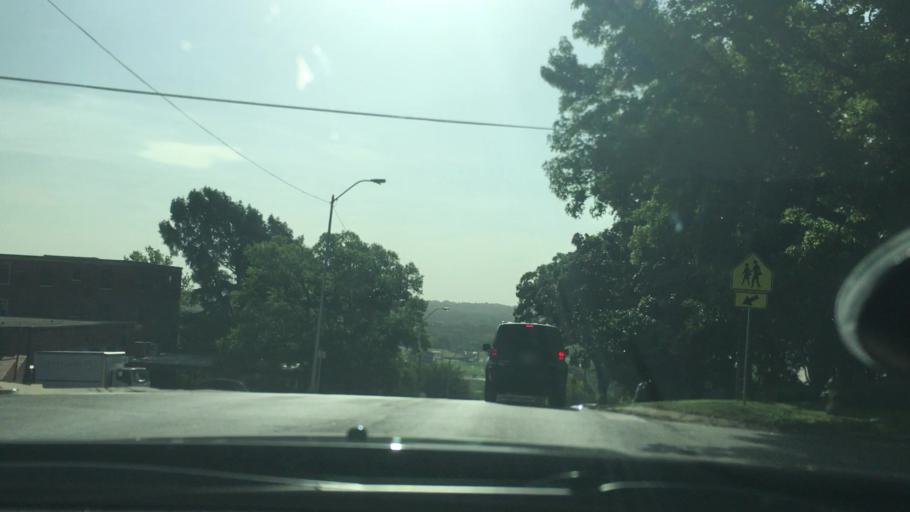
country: US
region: Oklahoma
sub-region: Pontotoc County
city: Ada
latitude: 34.7714
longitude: -96.6644
